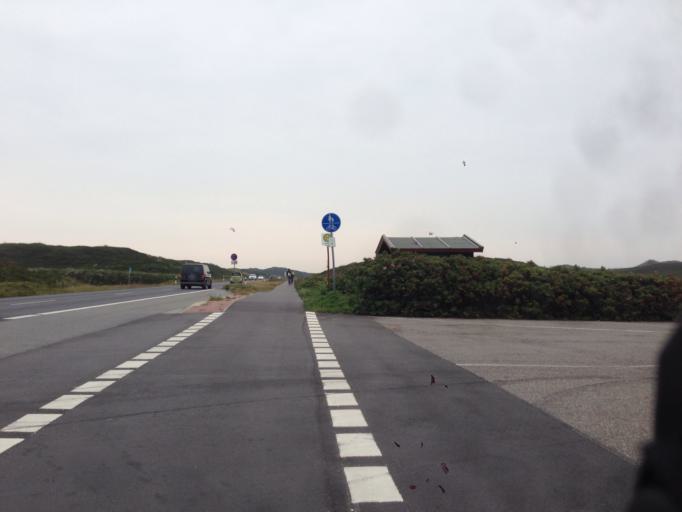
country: DE
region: Schleswig-Holstein
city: Norddorf
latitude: 54.7893
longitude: 8.2882
